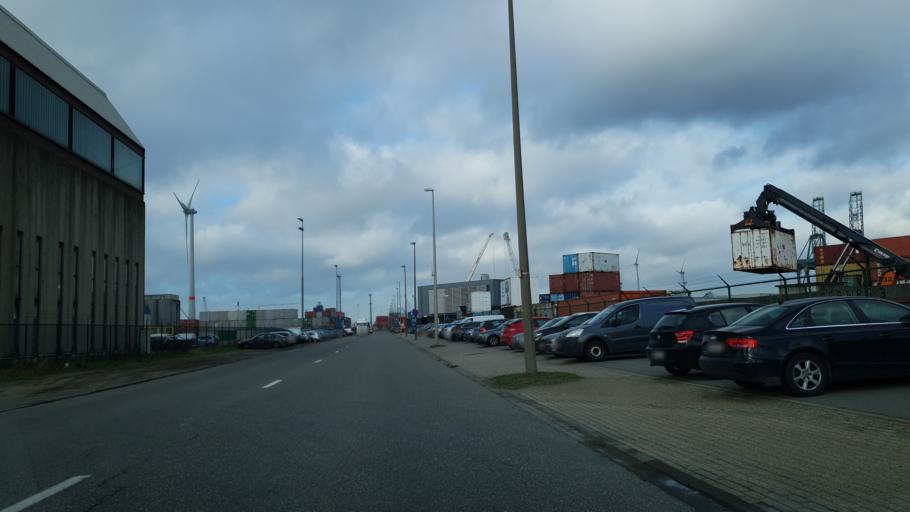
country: BE
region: Flanders
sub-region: Provincie Antwerpen
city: Stabroek
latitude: 51.2735
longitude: 4.3669
